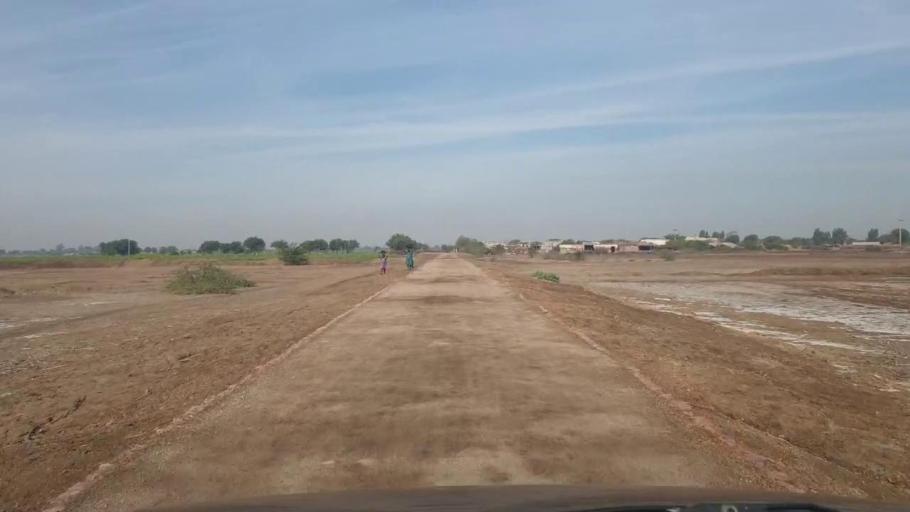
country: PK
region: Sindh
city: Umarkot
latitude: 25.3543
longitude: 69.6779
